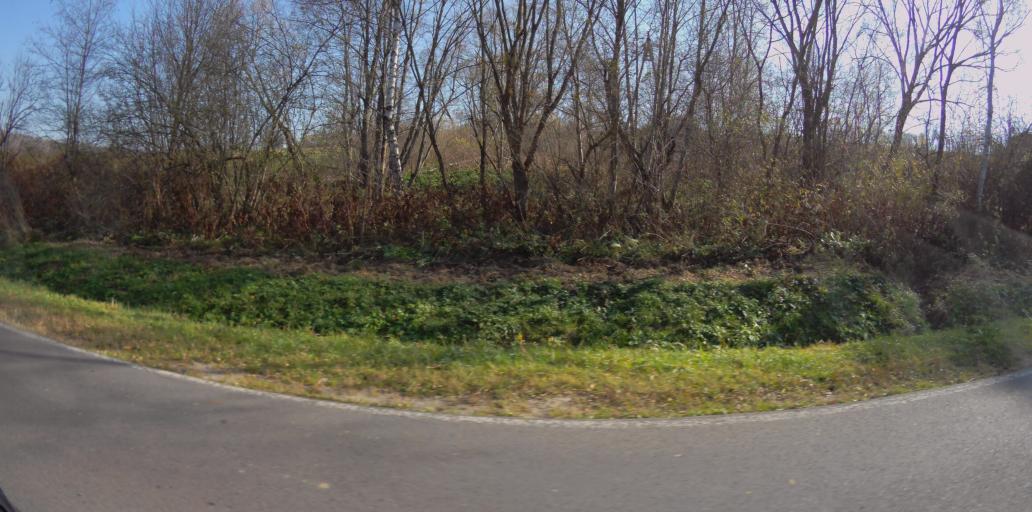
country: PL
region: Subcarpathian Voivodeship
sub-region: Powiat bieszczadzki
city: Lutowiska
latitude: 49.2084
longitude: 22.6782
